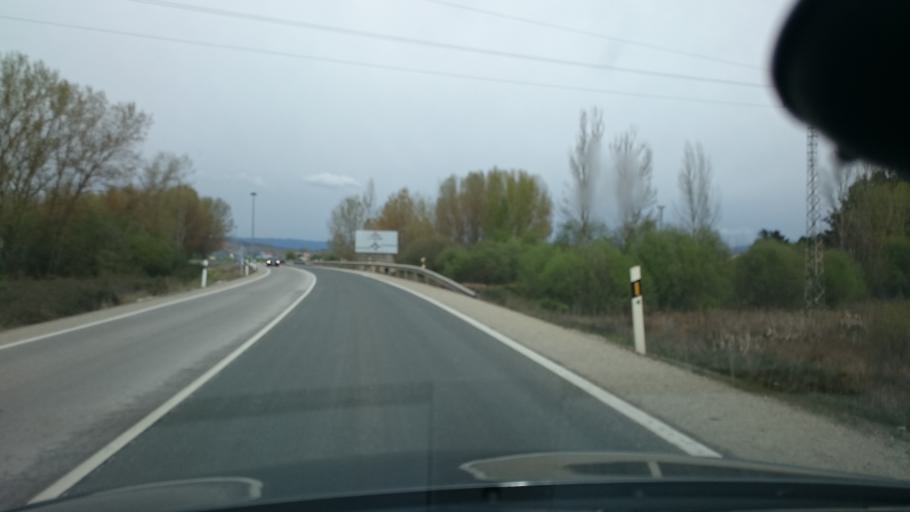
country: ES
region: Castille and Leon
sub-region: Provincia de Leon
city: Camponaraya
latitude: 42.5619
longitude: -6.6512
